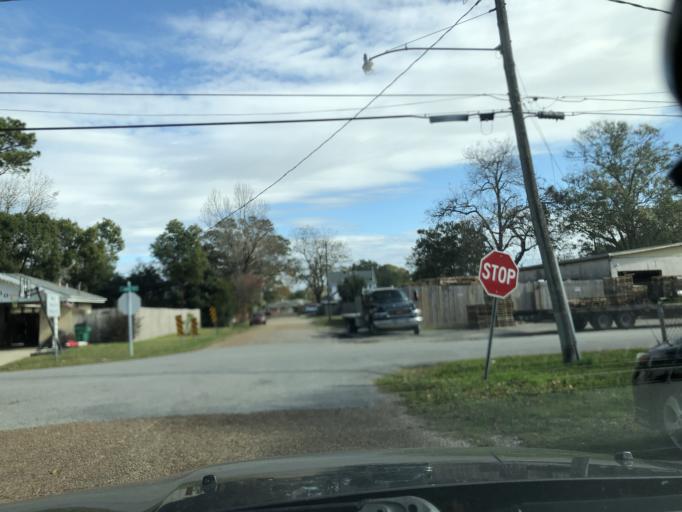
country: US
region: Louisiana
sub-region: Jefferson Parish
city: Metairie Terrace
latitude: 29.9831
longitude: -90.1690
